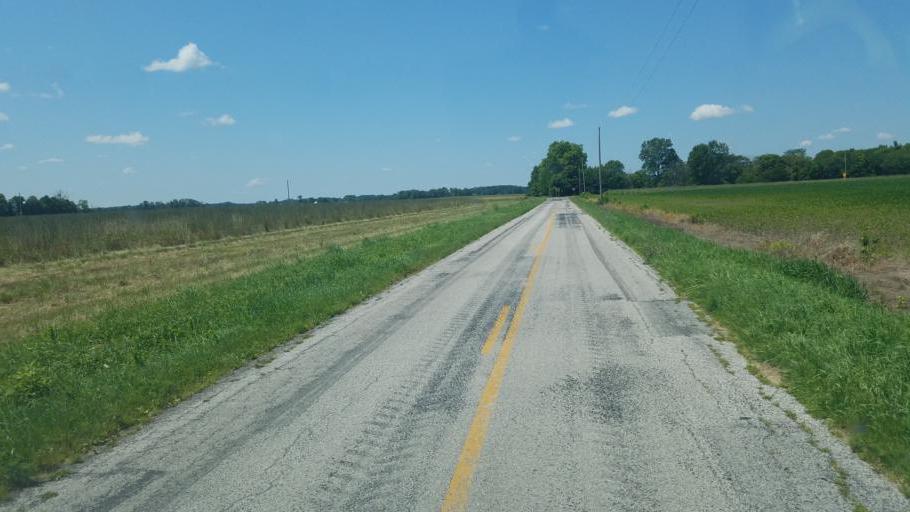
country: US
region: Ohio
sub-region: Union County
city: Richwood
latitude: 40.5601
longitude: -83.3065
